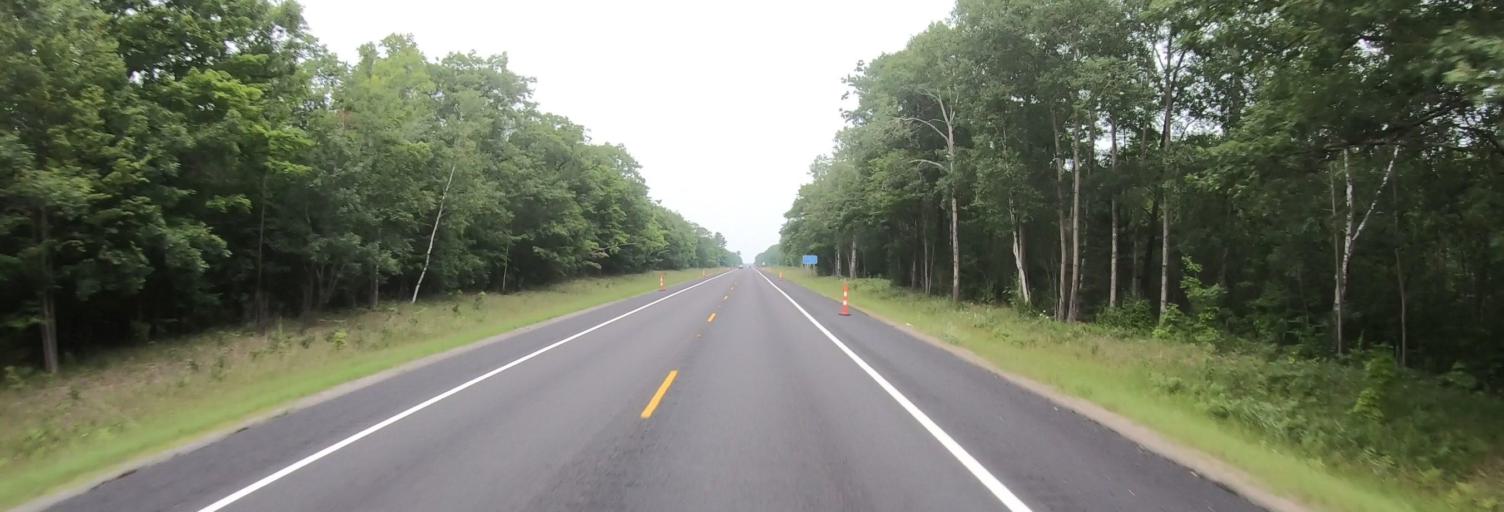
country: US
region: Michigan
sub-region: Mackinac County
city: Saint Ignace
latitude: 45.7054
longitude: -84.7674
